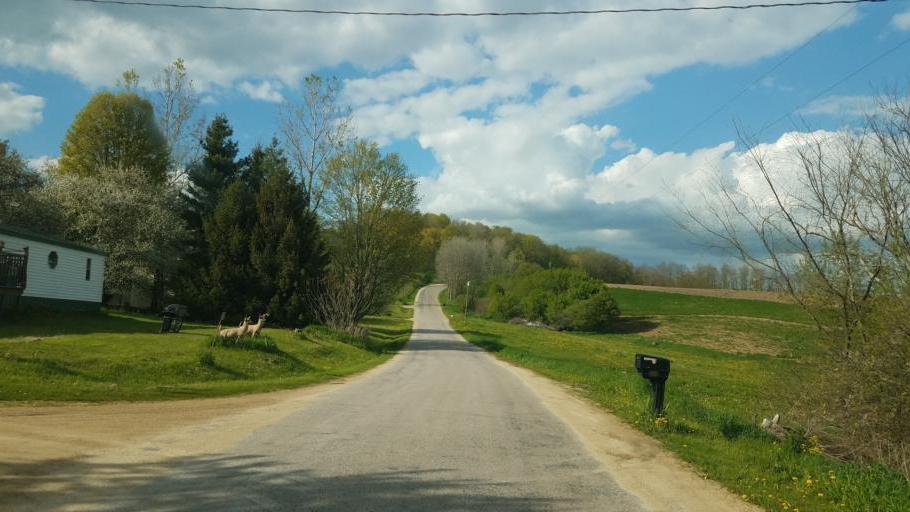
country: US
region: Wisconsin
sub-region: Vernon County
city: Hillsboro
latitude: 43.6399
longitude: -90.3683
